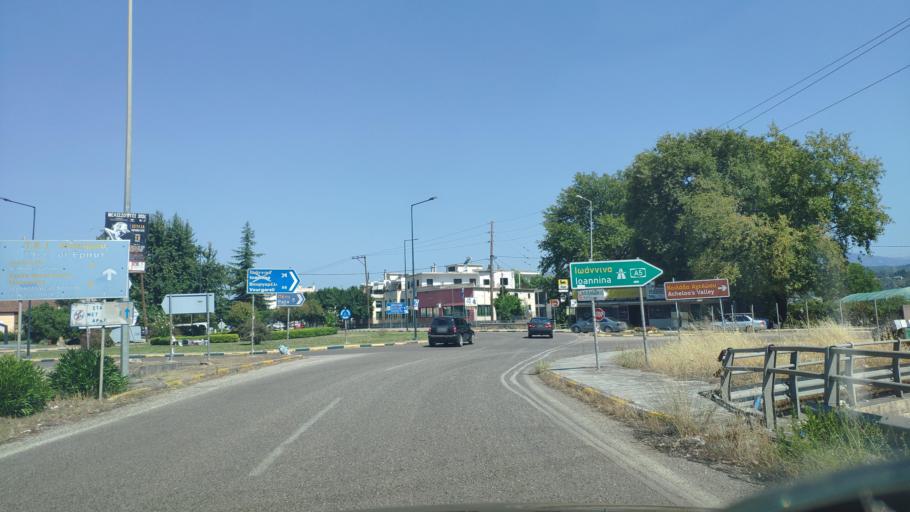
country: GR
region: Epirus
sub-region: Nomos Artas
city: Arta
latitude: 39.1549
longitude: 21.0035
